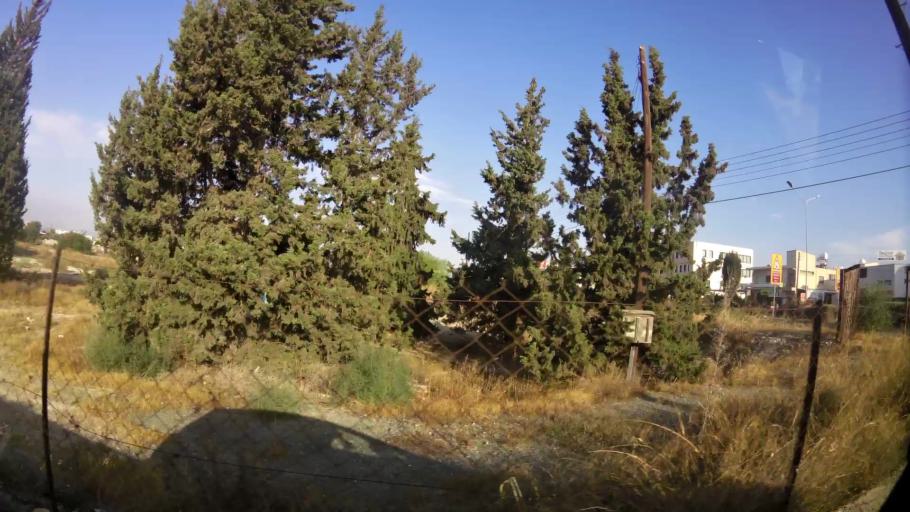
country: CY
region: Larnaka
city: Aradippou
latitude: 34.9309
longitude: 33.5983
